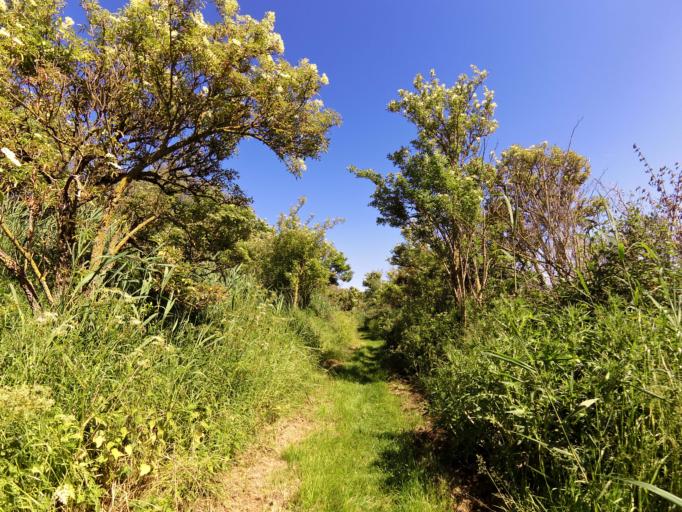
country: NL
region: South Holland
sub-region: Gemeente Goeree-Overflakkee
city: Goedereede
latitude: 51.8206
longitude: 4.0278
